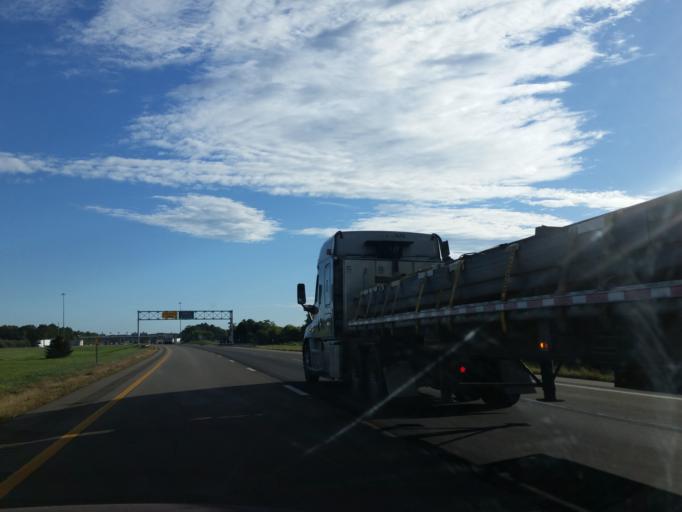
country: US
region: Pennsylvania
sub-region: Erie County
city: North East
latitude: 42.2622
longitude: -79.7434
